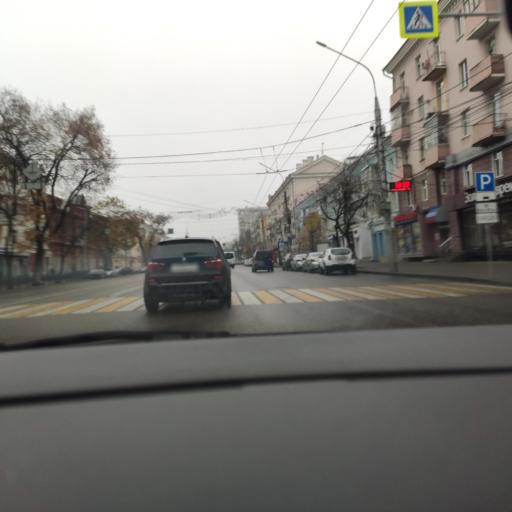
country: RU
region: Voronezj
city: Voronezh
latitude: 51.6654
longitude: 39.1955
